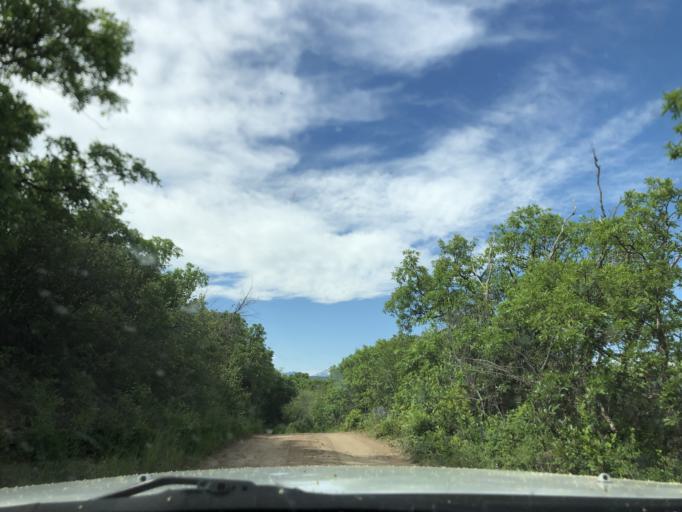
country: US
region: Colorado
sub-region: Delta County
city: Paonia
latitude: 39.0321
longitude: -107.3413
